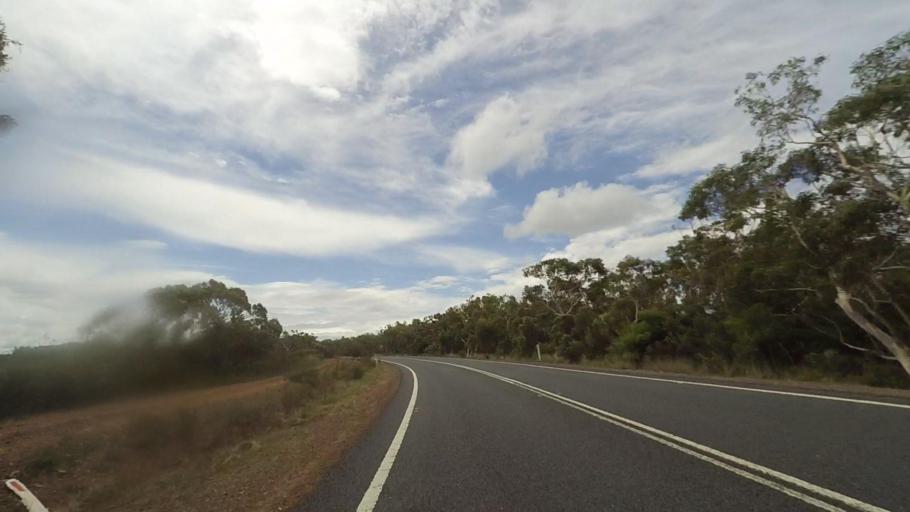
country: AU
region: New South Wales
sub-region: Sutherland Shire
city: Heathcote
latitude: -34.1060
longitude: 151.0600
